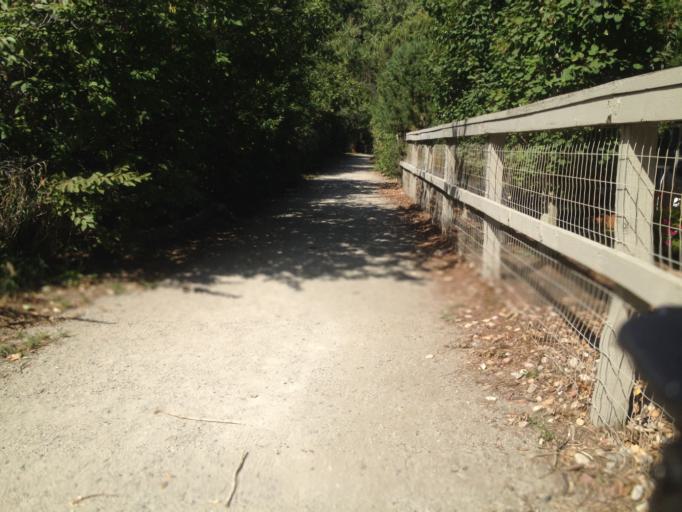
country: US
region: Colorado
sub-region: Boulder County
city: Louisville
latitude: 39.9928
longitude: -105.1214
